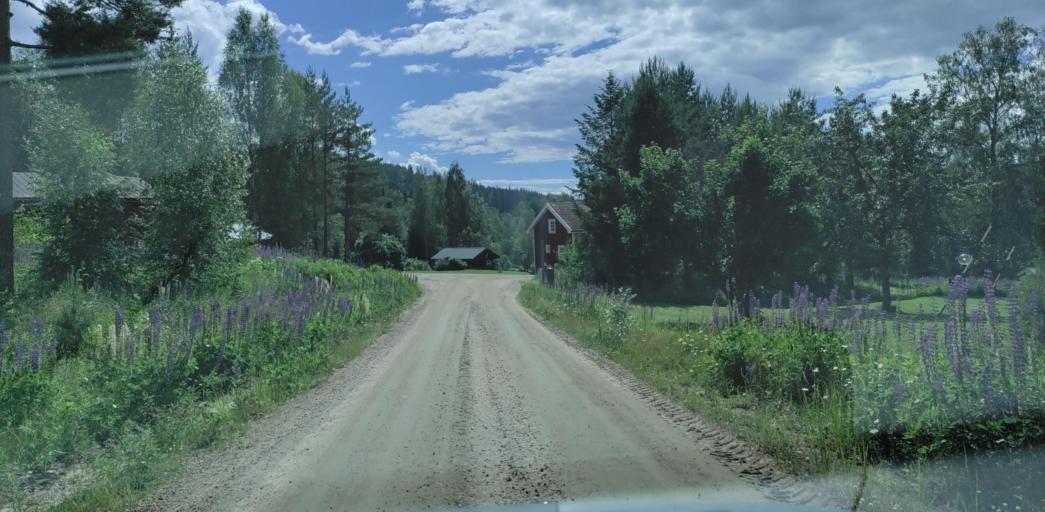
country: SE
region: Vaermland
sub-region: Sunne Kommun
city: Sunne
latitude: 60.0367
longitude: 13.2436
